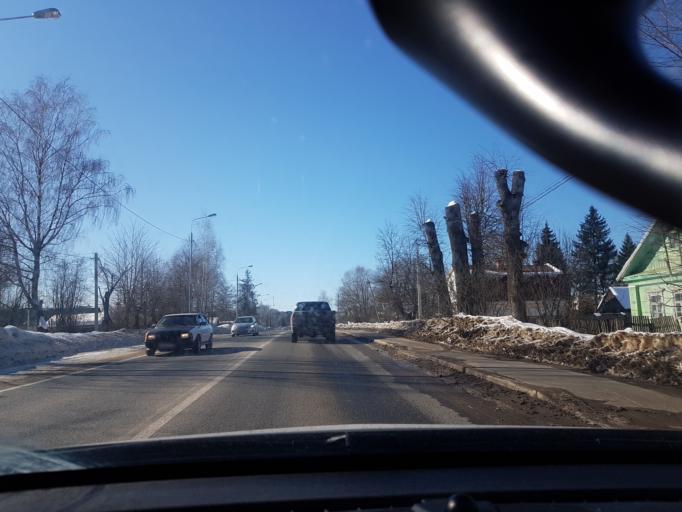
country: RU
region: Moskovskaya
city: Kostrovo
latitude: 55.9167
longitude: 36.6847
